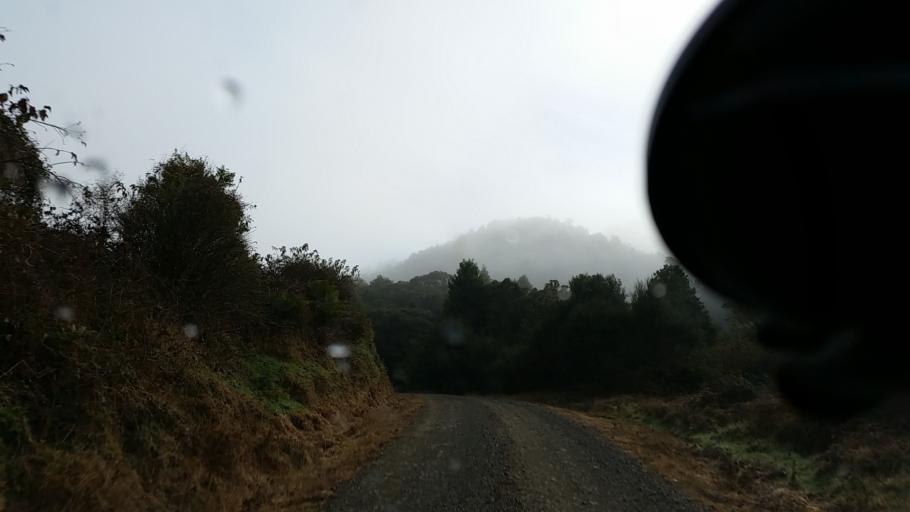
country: NZ
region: Taranaki
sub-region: New Plymouth District
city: Waitara
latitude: -38.9662
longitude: 174.7938
